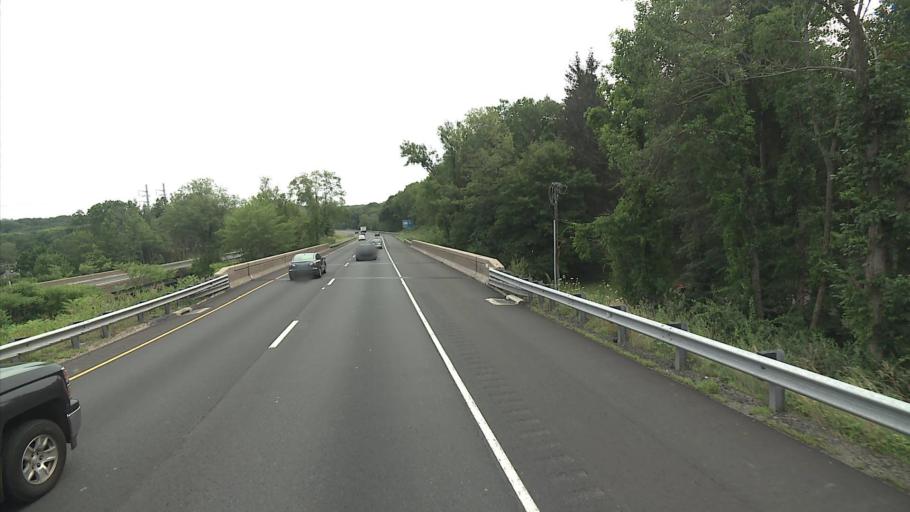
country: US
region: Connecticut
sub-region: New Haven County
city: Middlebury
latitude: 41.5213
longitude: -73.0947
